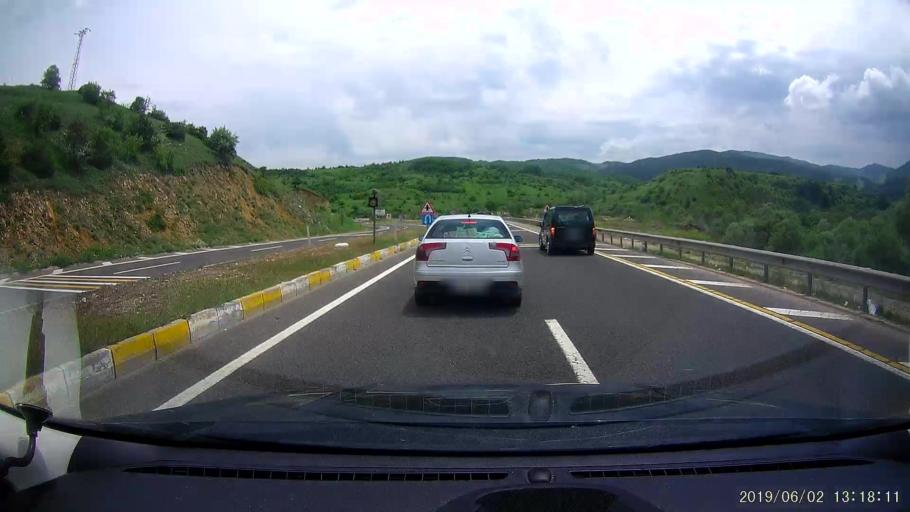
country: TR
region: Karabuk
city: Gozyeri
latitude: 40.8357
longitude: 32.7152
